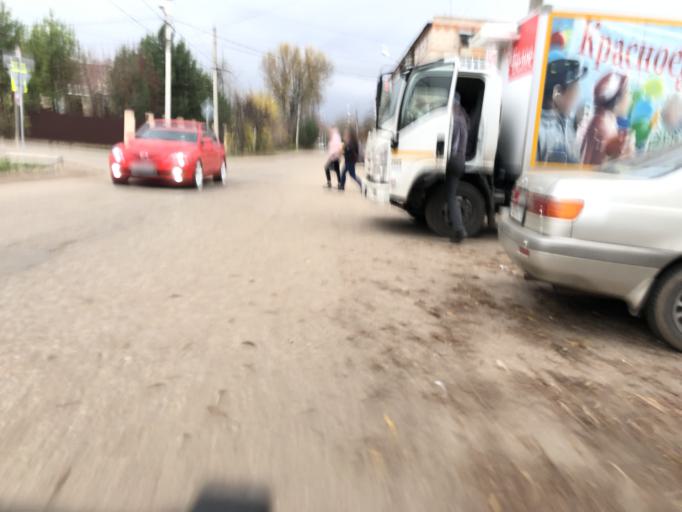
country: RU
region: Tverskaya
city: Rzhev
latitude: 56.2480
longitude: 34.3308
